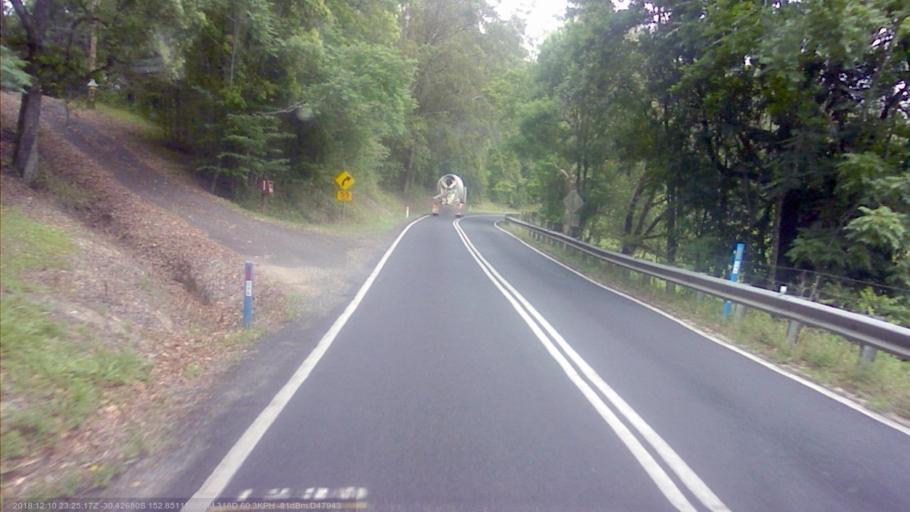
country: AU
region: New South Wales
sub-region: Bellingen
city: Bellingen
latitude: -30.4268
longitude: 152.8511
